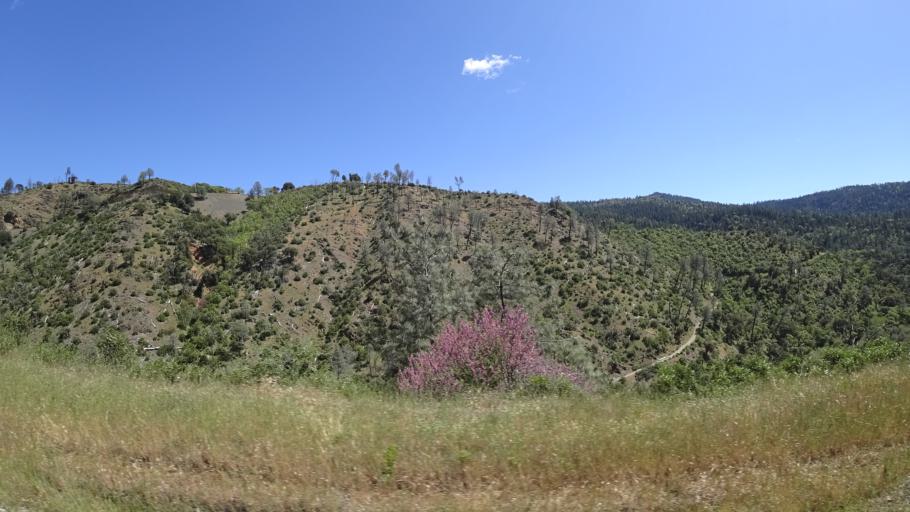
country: US
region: California
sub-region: Trinity County
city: Weaverville
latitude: 40.7389
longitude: -123.0058
